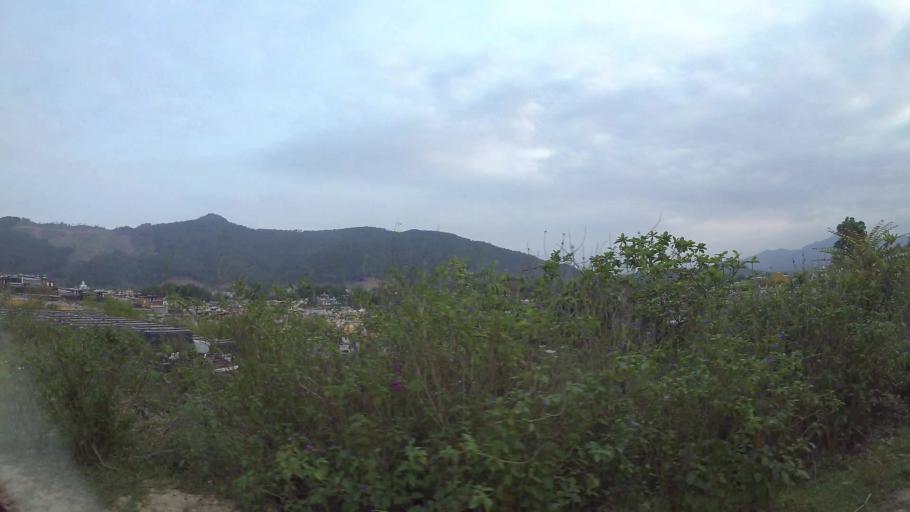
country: VN
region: Da Nang
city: Lien Chieu
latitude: 16.0625
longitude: 108.1188
